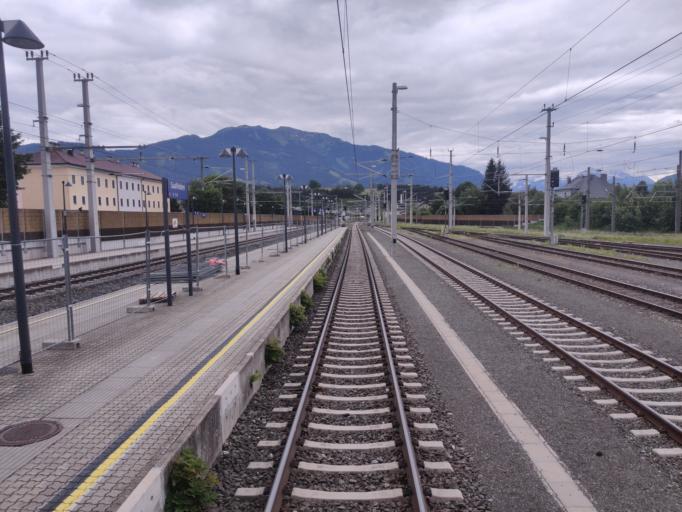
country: AT
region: Salzburg
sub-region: Politischer Bezirk Zell am See
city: Saalfelden am Steinernen Meer
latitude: 47.4262
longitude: 12.8298
